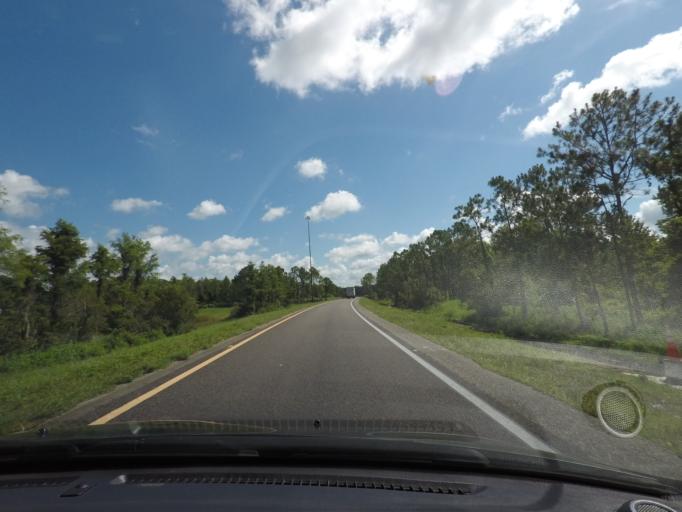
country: US
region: Florida
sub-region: Orange County
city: Conway
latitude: 28.4471
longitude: -81.2291
